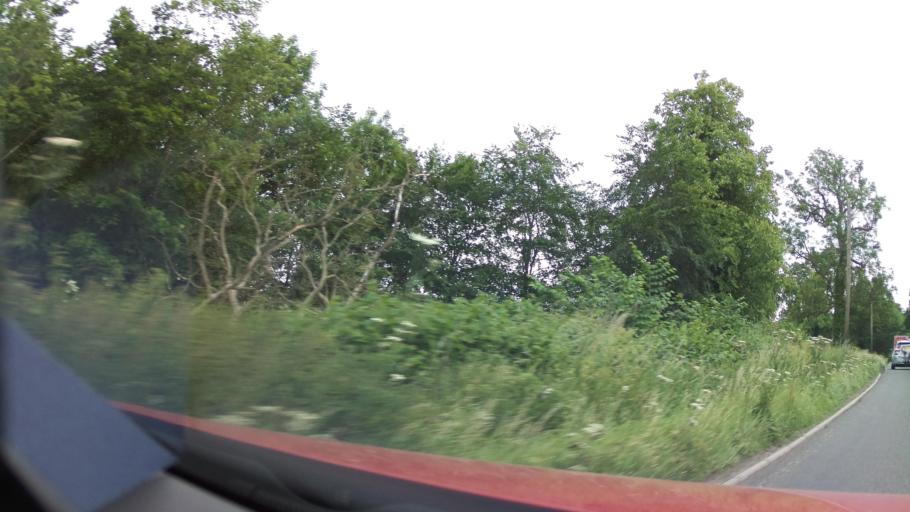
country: GB
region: England
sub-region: Derbyshire
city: Rodsley
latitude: 52.9052
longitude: -1.7662
